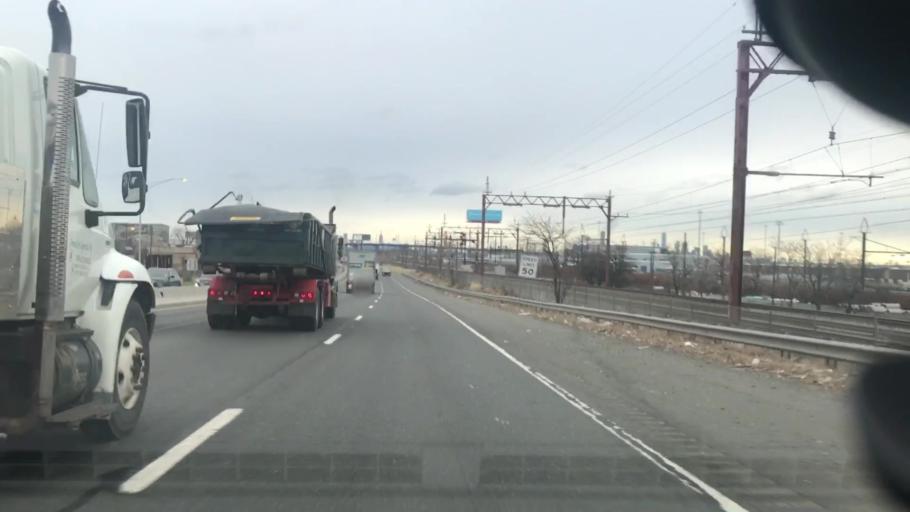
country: US
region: New Jersey
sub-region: Hudson County
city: Harrison
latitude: 40.7422
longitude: -74.1527
